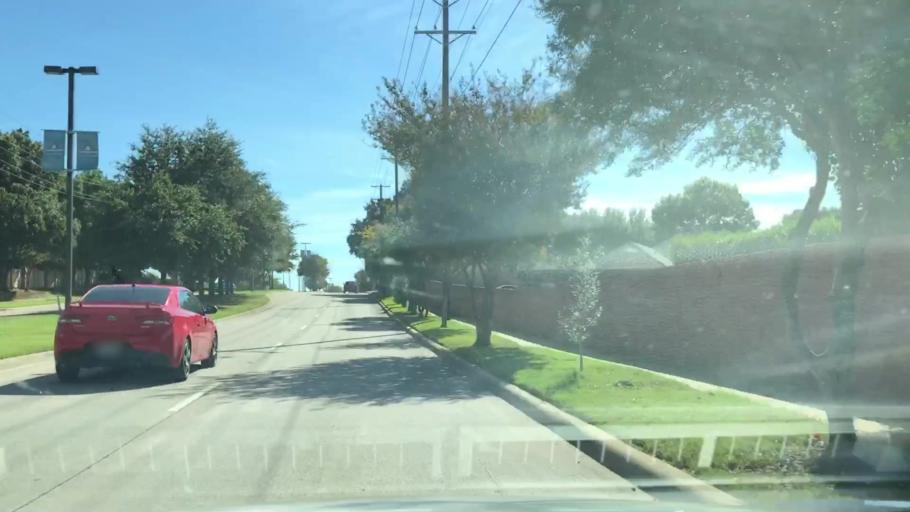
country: US
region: Texas
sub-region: Dallas County
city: Addison
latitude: 33.0160
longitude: -96.8575
